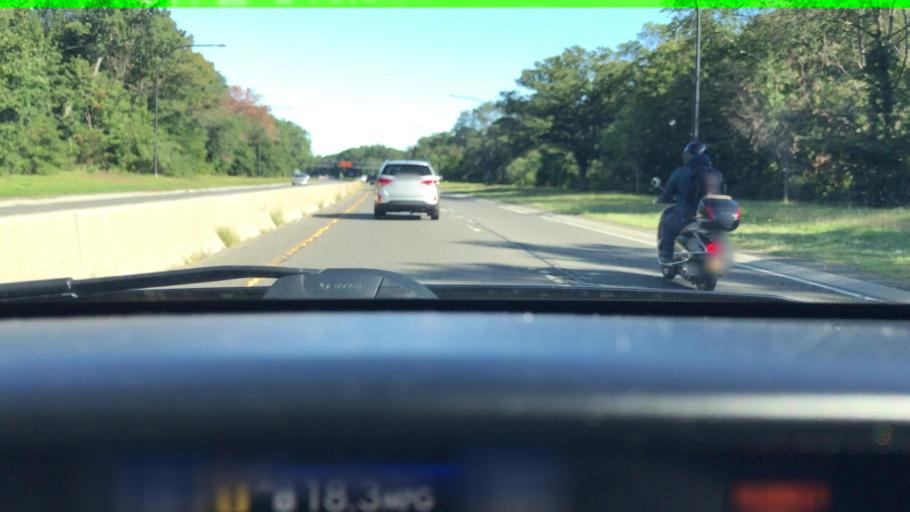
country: US
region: New York
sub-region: Nassau County
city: Salisbury
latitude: 40.7382
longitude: -73.5440
